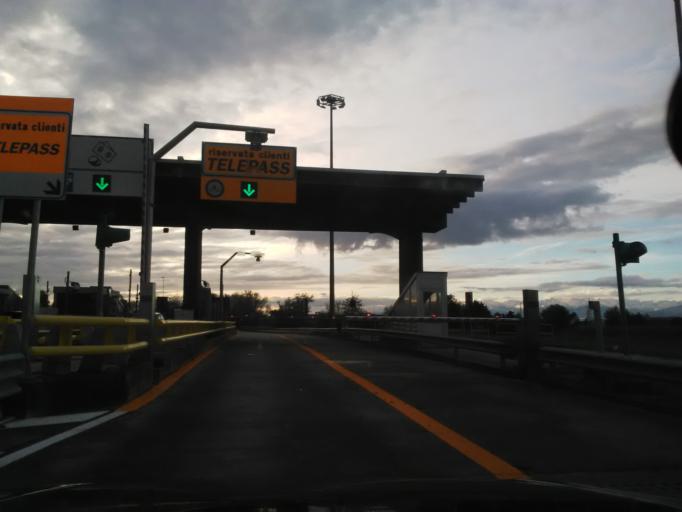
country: IT
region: Piedmont
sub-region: Provincia di Novara
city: Vicolungo
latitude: 45.4680
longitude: 8.4690
